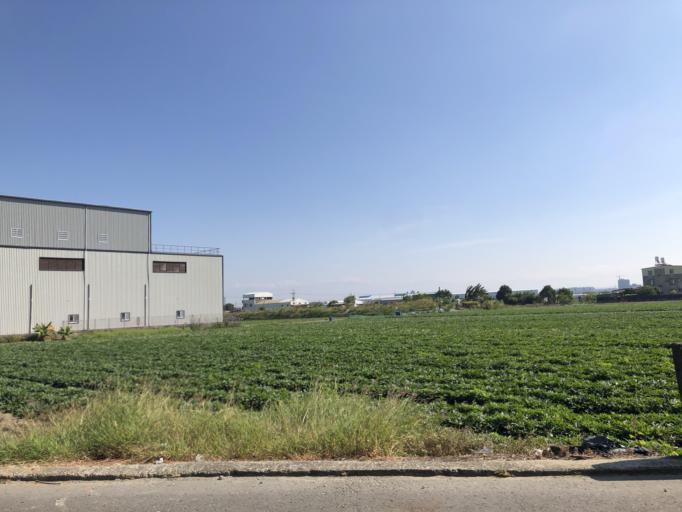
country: TW
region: Taiwan
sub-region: Tainan
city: Tainan
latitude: 23.0206
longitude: 120.2893
